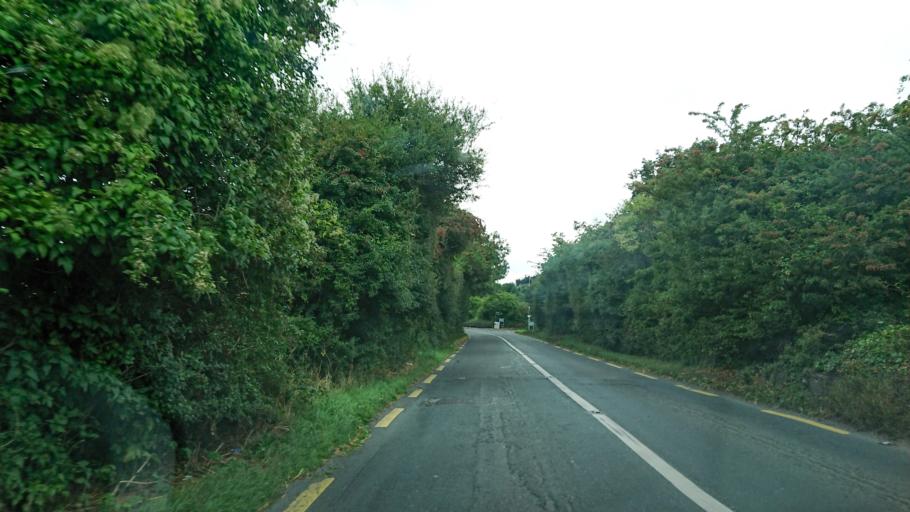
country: IE
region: Munster
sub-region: County Cork
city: Mallow
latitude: 52.1478
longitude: -8.6352
